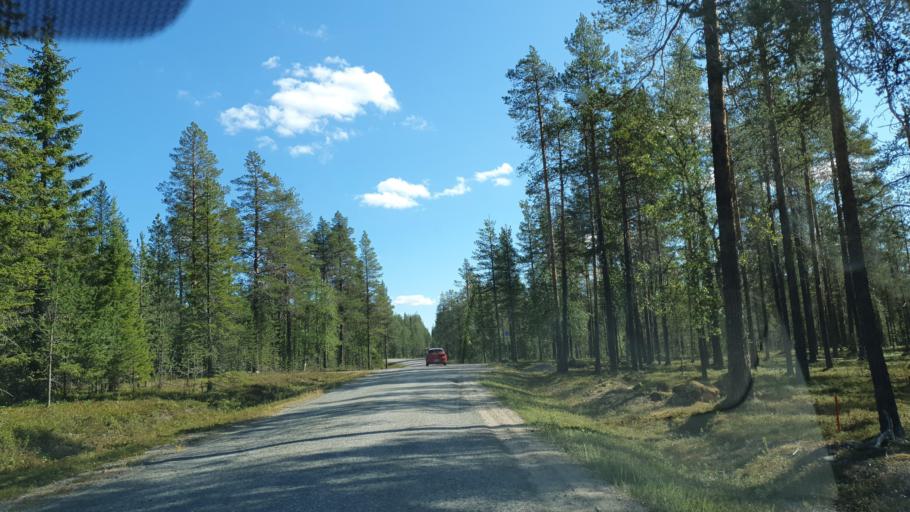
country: FI
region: Lapland
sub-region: Tunturi-Lappi
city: Muonio
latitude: 67.7065
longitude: 24.1391
